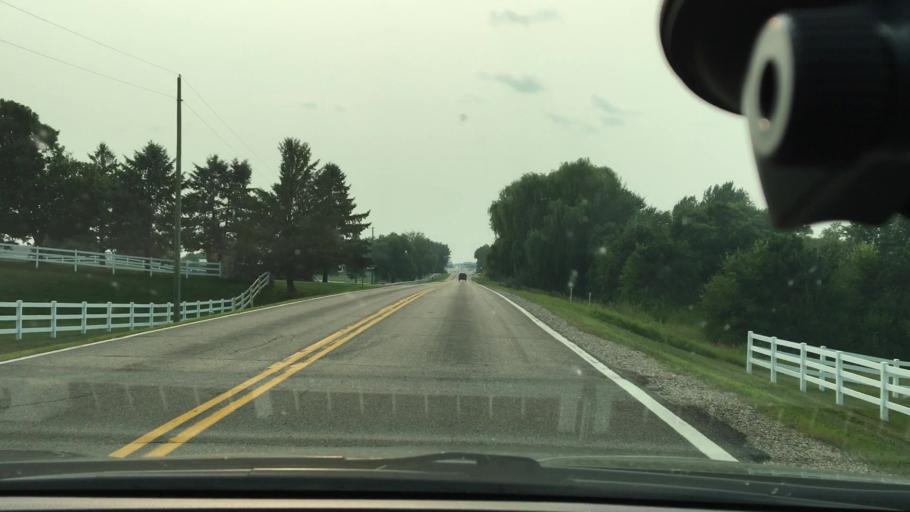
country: US
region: Minnesota
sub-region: Hennepin County
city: Dayton
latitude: 45.2523
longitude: -93.5412
